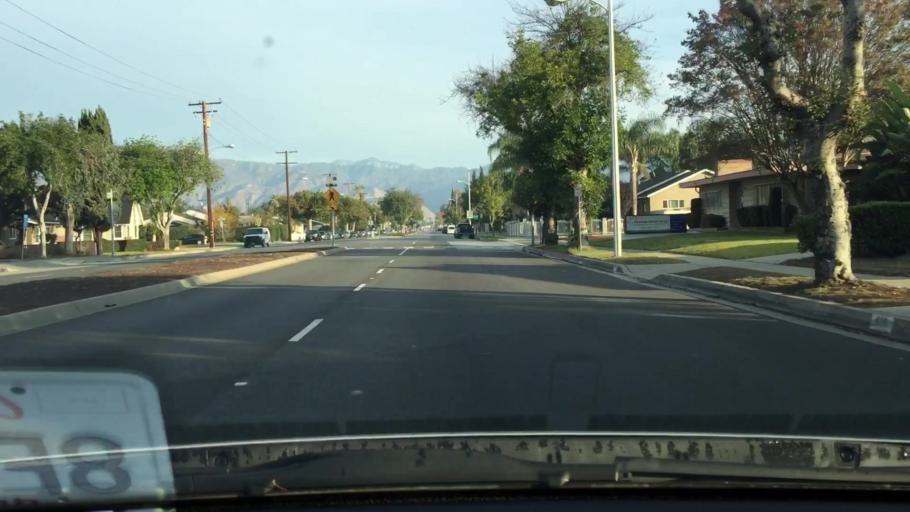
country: US
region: California
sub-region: Los Angeles County
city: West Covina
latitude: 34.0786
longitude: -117.9349
